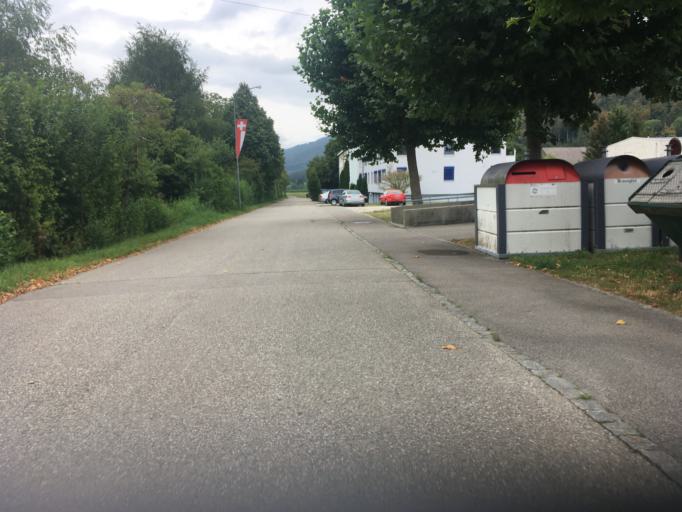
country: CH
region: Solothurn
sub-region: Bezirk Thal
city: Matzendorf
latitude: 47.2959
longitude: 7.5966
